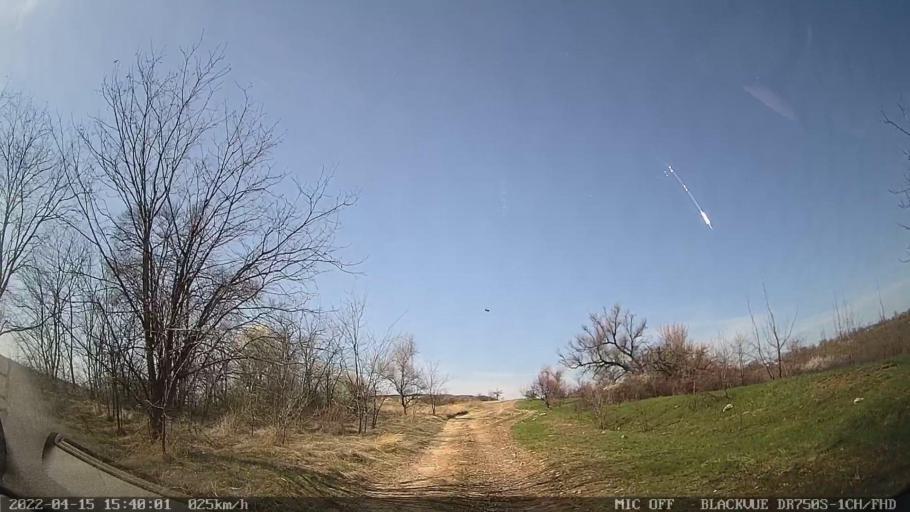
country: MD
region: Raionul Ocnita
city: Otaci
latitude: 48.3549
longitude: 27.9261
